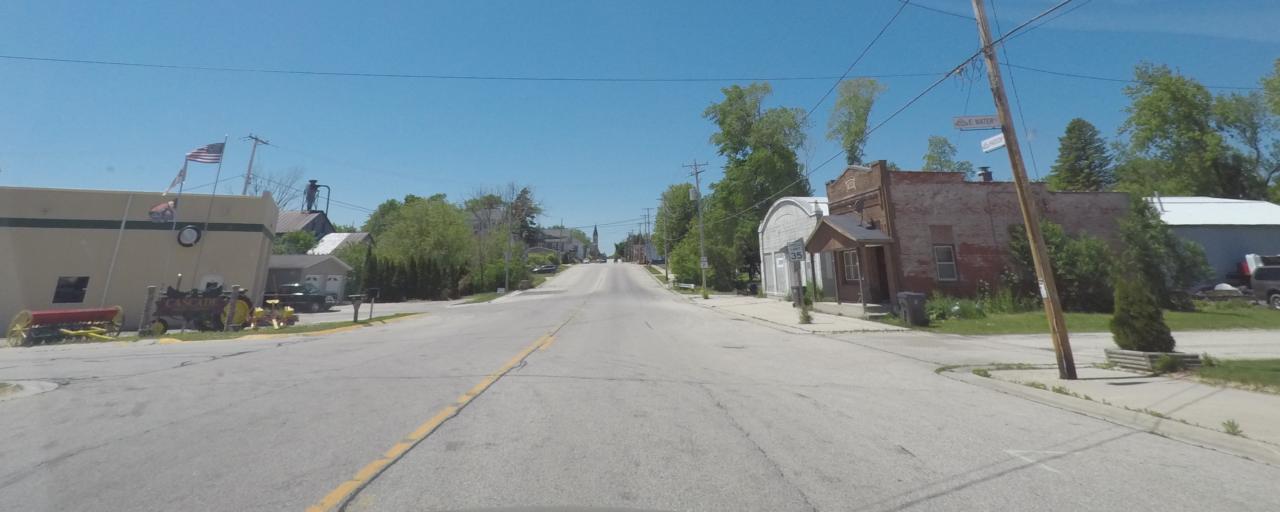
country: US
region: Wisconsin
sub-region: Sheboygan County
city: Plymouth
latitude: 43.6584
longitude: -88.0066
